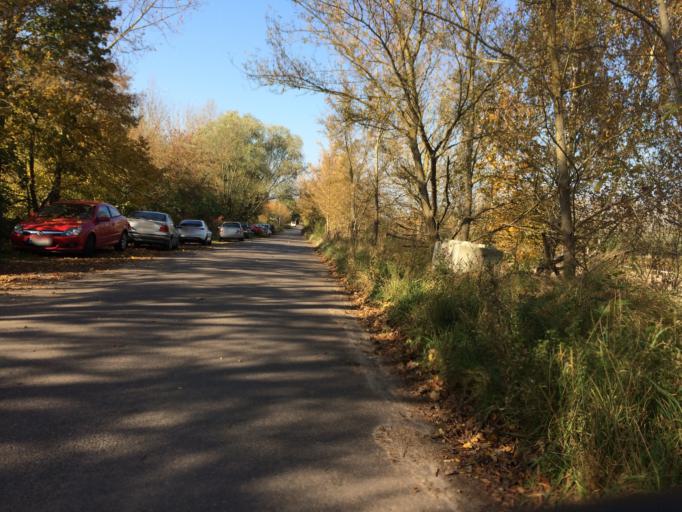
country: DE
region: Berlin
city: Blankenfelde
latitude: 52.6383
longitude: 13.4149
